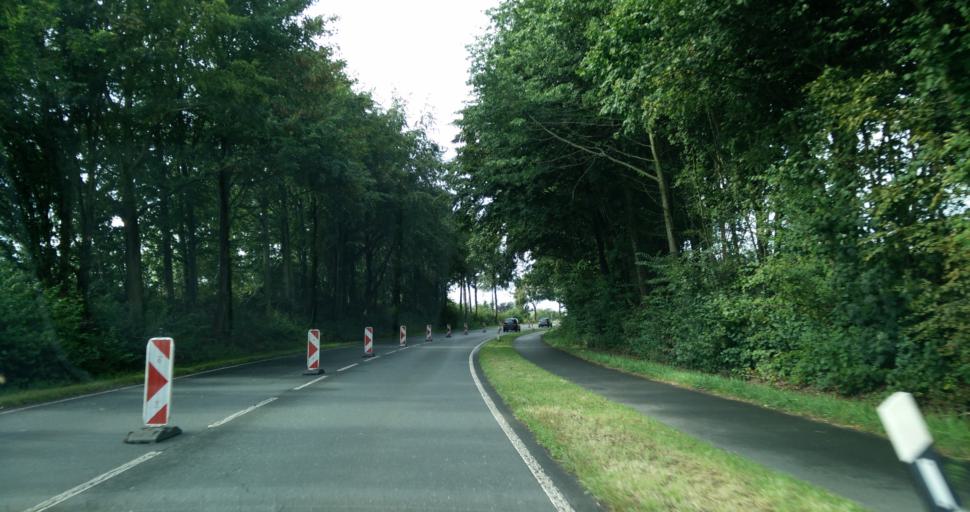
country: DE
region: North Rhine-Westphalia
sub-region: Regierungsbezirk Dusseldorf
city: Mettmann
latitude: 51.2427
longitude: 6.9509
